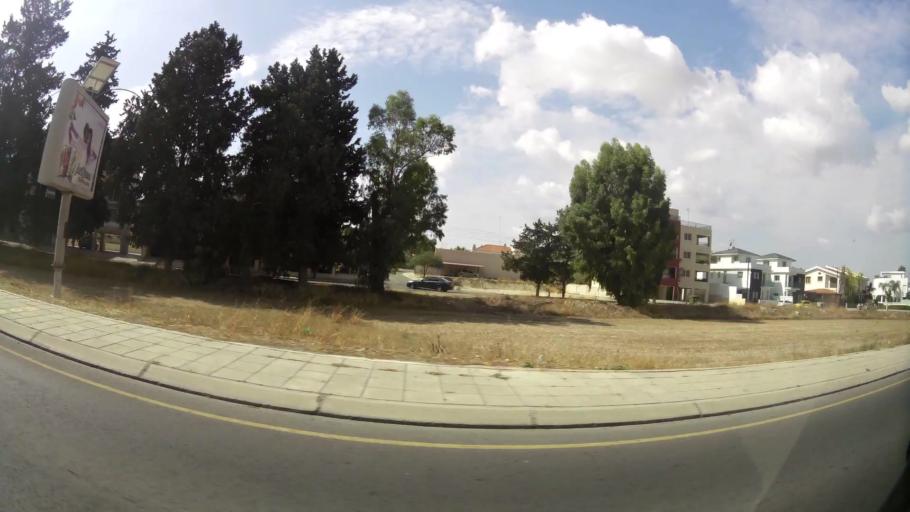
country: CY
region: Larnaka
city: Aradippou
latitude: 34.9462
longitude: 33.5783
